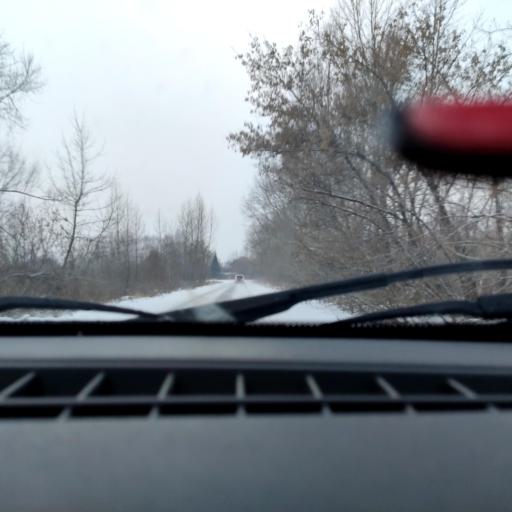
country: RU
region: Bashkortostan
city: Blagoveshchensk
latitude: 54.9051
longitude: 56.0124
